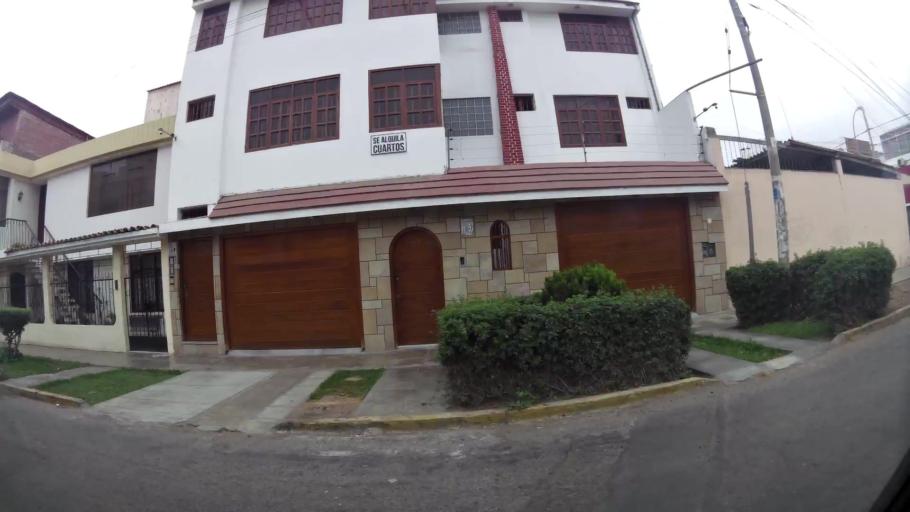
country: PE
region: La Libertad
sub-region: Provincia de Trujillo
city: Trujillo
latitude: -8.1205
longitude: -79.0309
